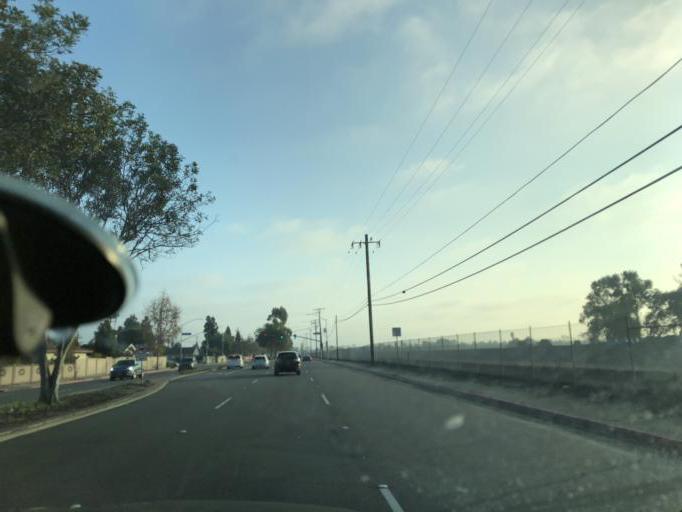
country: US
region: California
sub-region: Orange County
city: Westminster
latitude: 33.7385
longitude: -118.0418
